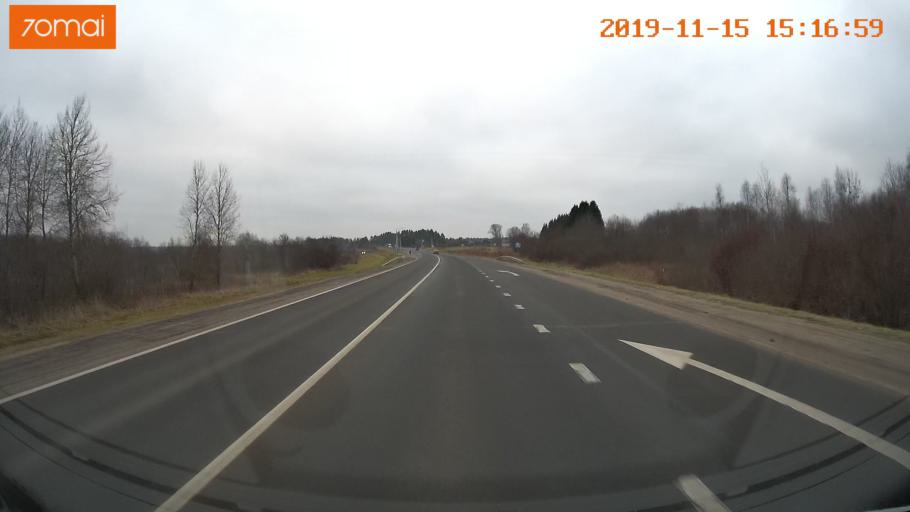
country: RU
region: Jaroslavl
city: Danilov
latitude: 58.2674
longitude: 40.1855
